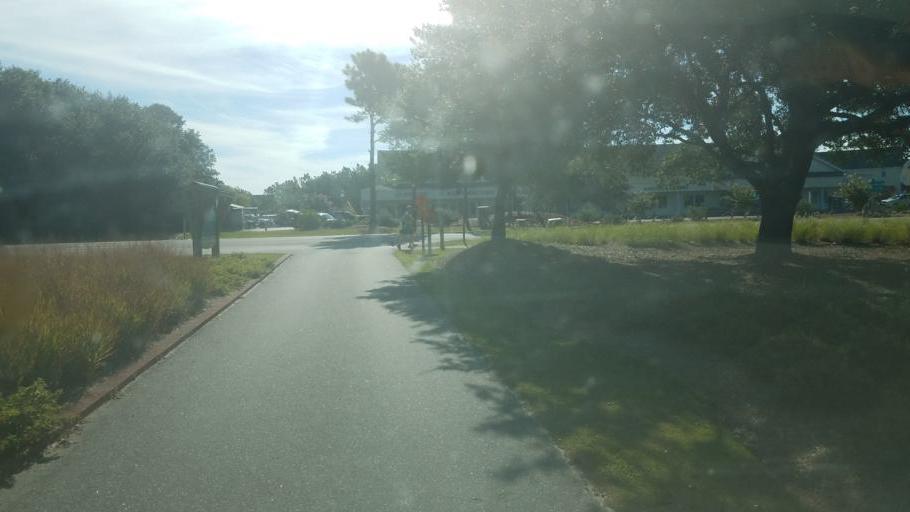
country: US
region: North Carolina
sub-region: Currituck County
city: Currituck
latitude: 36.3743
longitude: -75.8293
